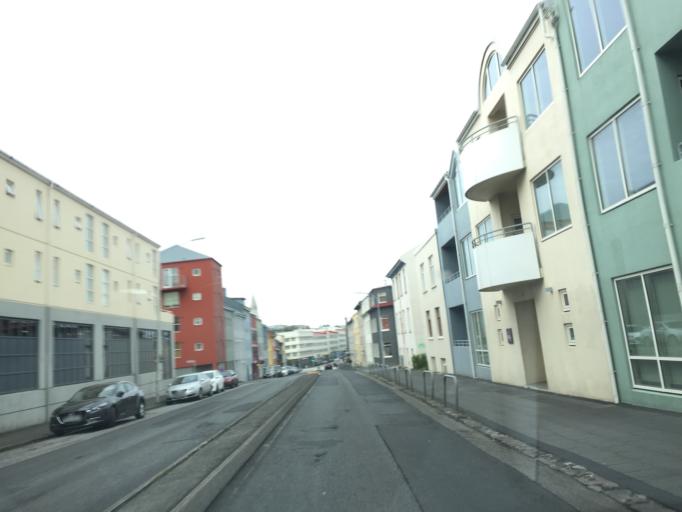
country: IS
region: Capital Region
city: Reykjavik
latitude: 64.1431
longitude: -21.9089
